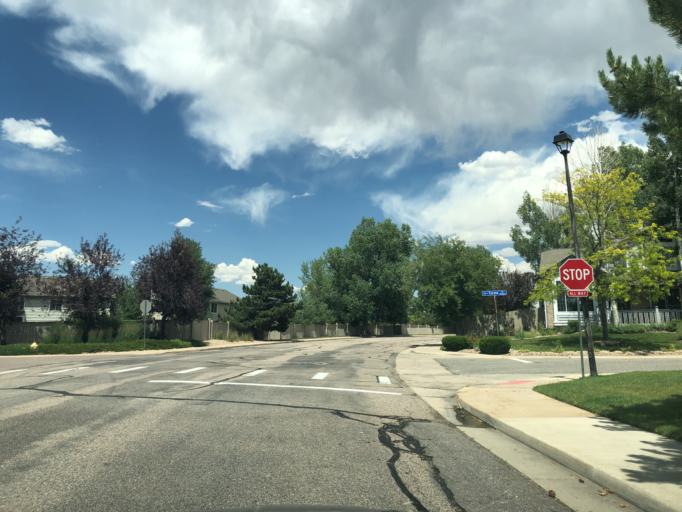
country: US
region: Colorado
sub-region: Arapahoe County
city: Dove Valley
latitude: 39.6222
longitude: -104.7612
